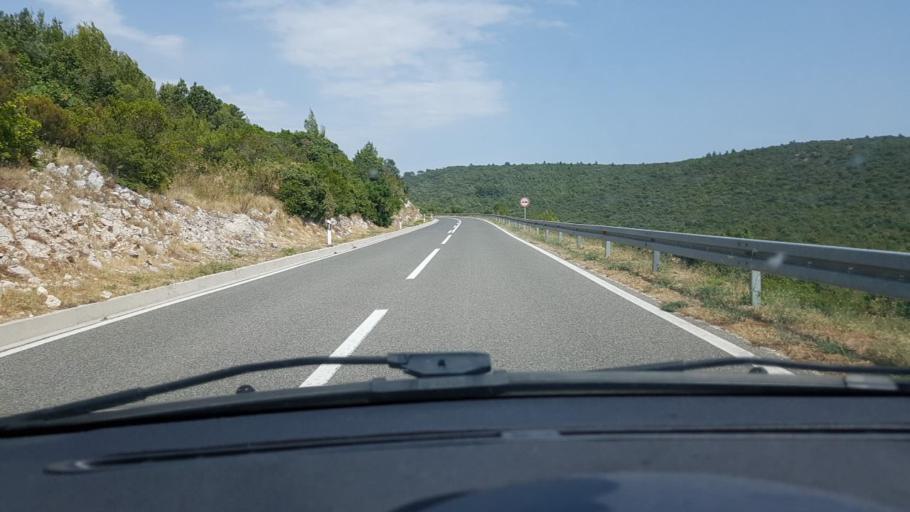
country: HR
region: Dubrovacko-Neretvanska
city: Smokvica
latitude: 42.9551
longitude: 16.9262
